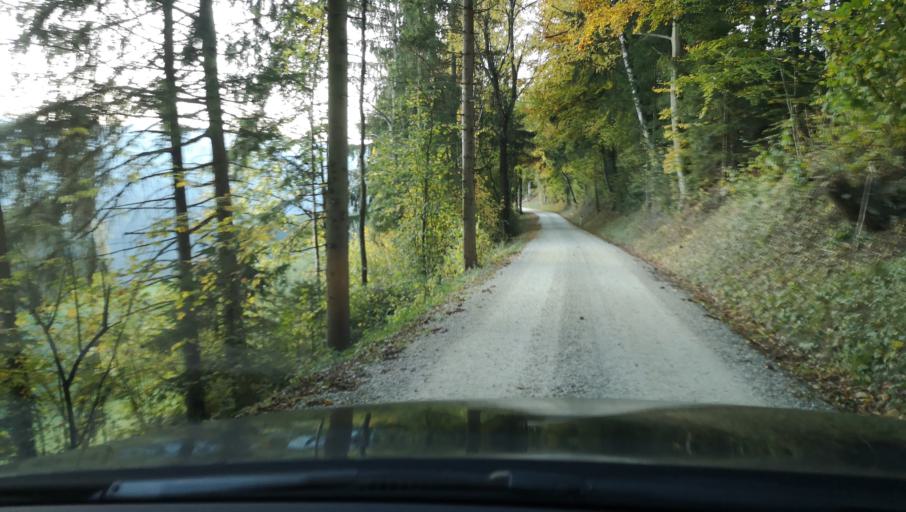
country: AT
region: Styria
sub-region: Politischer Bezirk Weiz
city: Birkfeld
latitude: 47.3567
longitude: 15.6767
